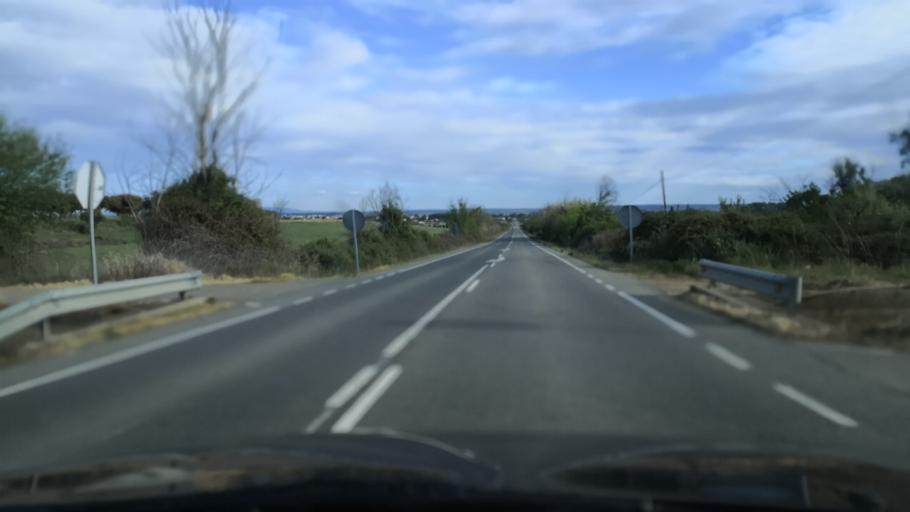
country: ES
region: Extremadura
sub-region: Provincia de Caceres
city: Moraleja
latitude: 40.0950
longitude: -6.6752
